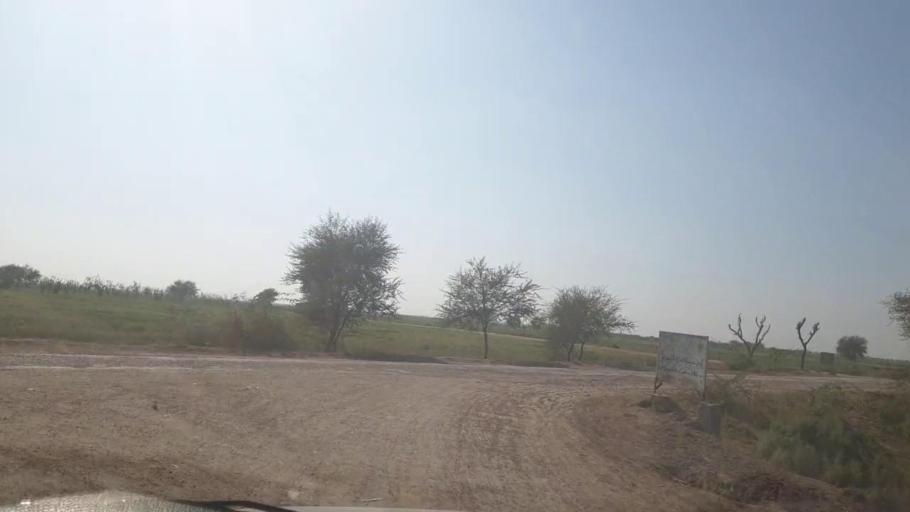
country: PK
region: Sindh
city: Mirpur Khas
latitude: 25.4521
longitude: 69.1128
